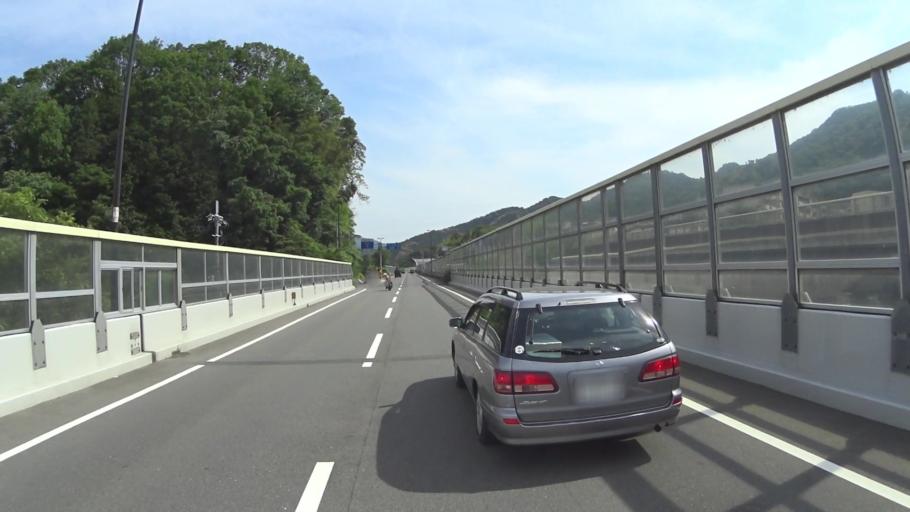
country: JP
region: Shiga Prefecture
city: Otsu-shi
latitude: 35.0311
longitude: 135.8503
